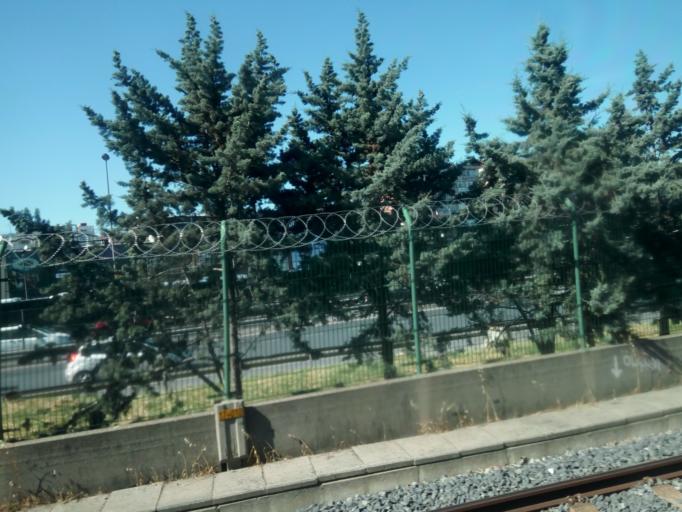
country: TR
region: Istanbul
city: Bahcelievler
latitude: 40.9912
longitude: 28.8470
